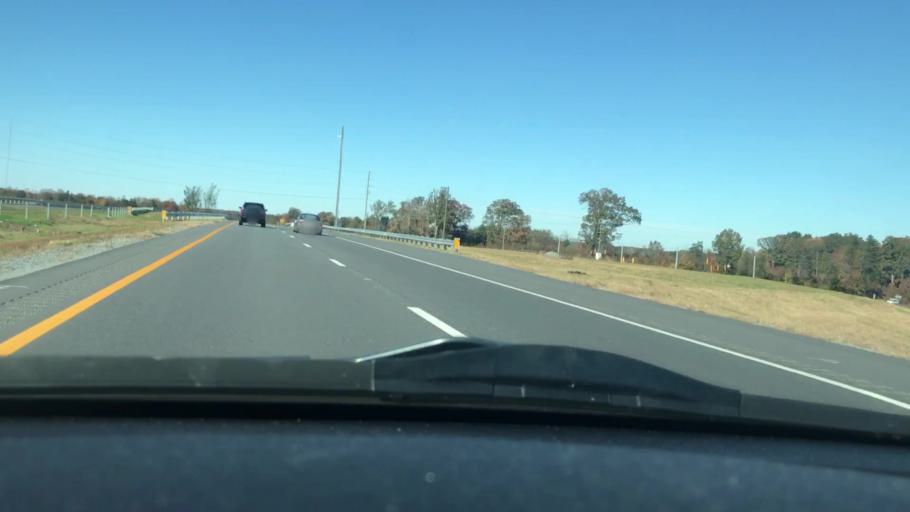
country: US
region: North Carolina
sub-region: Guilford County
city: Summerfield
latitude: 36.2455
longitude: -79.9204
